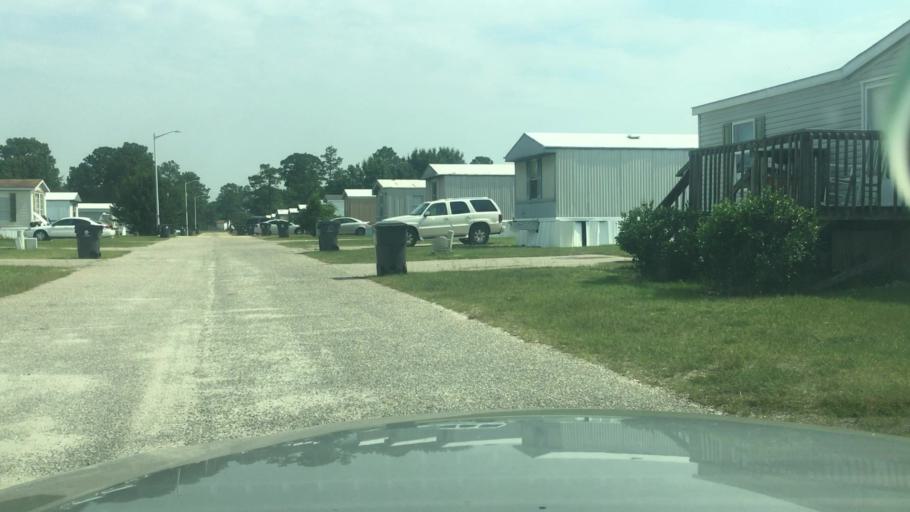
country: US
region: North Carolina
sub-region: Cumberland County
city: Hope Mills
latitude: 34.9970
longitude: -78.9511
